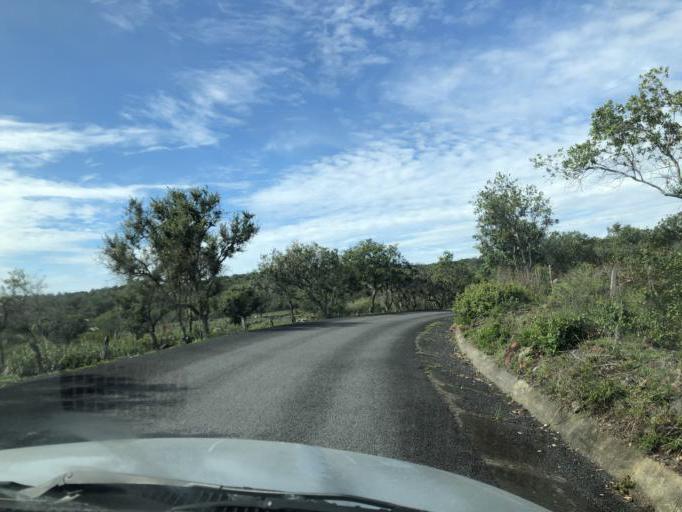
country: MX
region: Veracruz
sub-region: Alto Lucero de Gutierrez Barrios
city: Palma Sola
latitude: 19.7844
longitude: -96.5529
